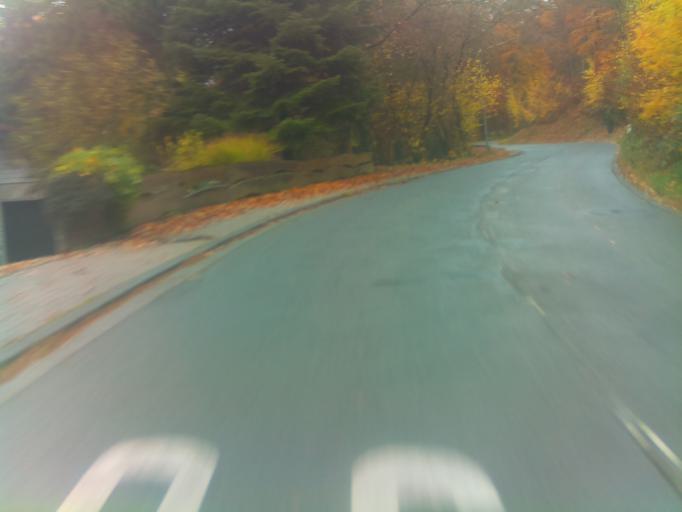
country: DE
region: Hesse
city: Neckarsteinach
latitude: 49.4078
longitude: 8.8442
